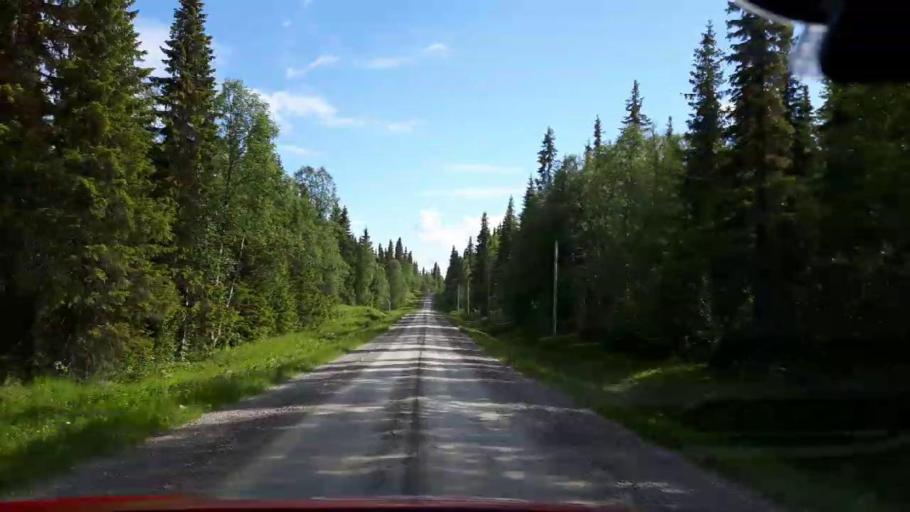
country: SE
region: Jaemtland
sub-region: Krokoms Kommun
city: Valla
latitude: 63.7973
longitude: 14.0461
